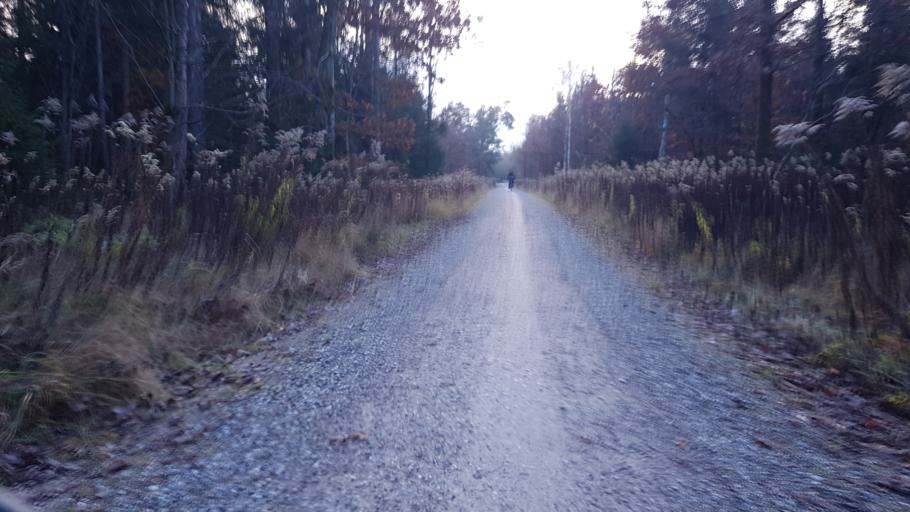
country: DE
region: Bavaria
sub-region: Upper Bavaria
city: Unterhaching
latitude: 48.0780
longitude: 11.5935
